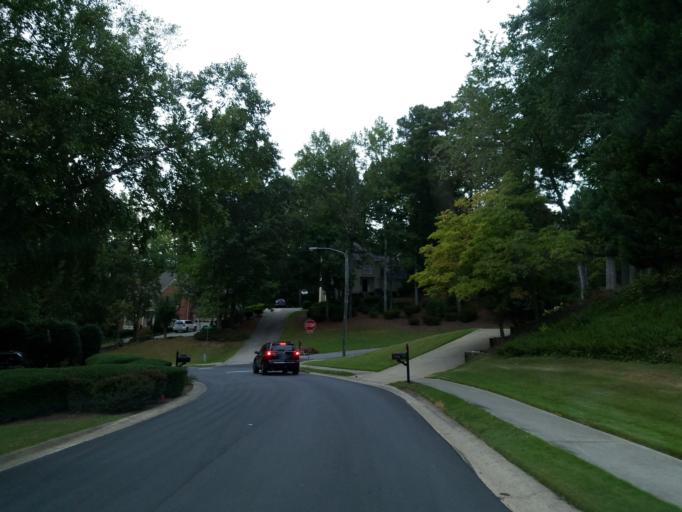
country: US
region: Georgia
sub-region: Fulton County
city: Sandy Springs
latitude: 33.9713
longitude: -84.4241
